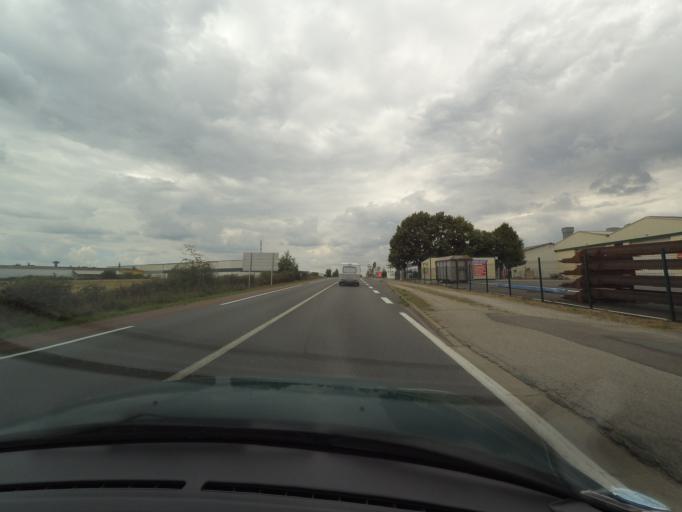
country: FR
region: Poitou-Charentes
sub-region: Departement des Deux-Sevres
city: Parthenay
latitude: 46.6661
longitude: -0.2526
